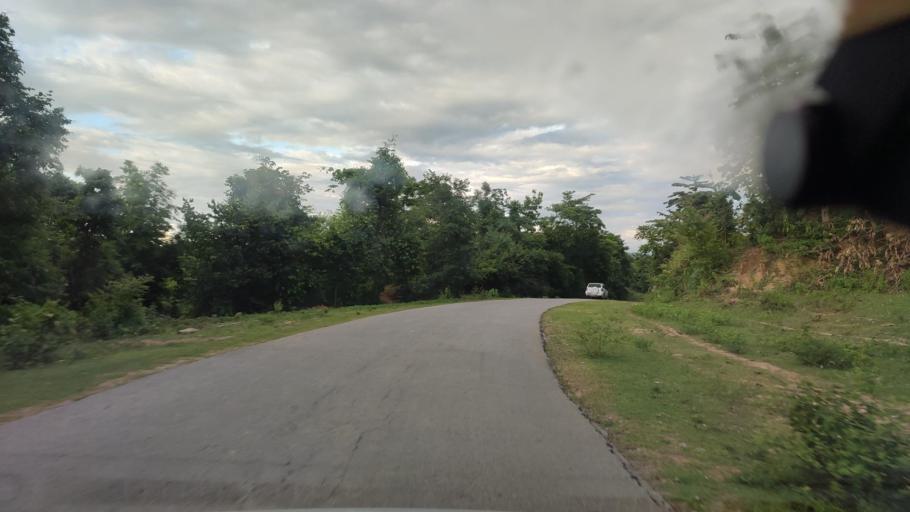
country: MM
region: Mandalay
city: Nay Pyi Taw
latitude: 19.9977
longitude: 95.9273
